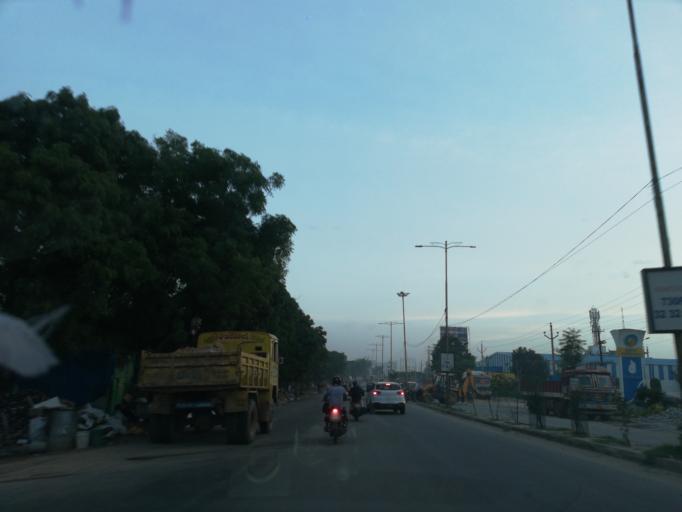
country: IN
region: Telangana
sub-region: Medak
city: Serilingampalle
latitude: 17.5369
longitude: 78.3585
